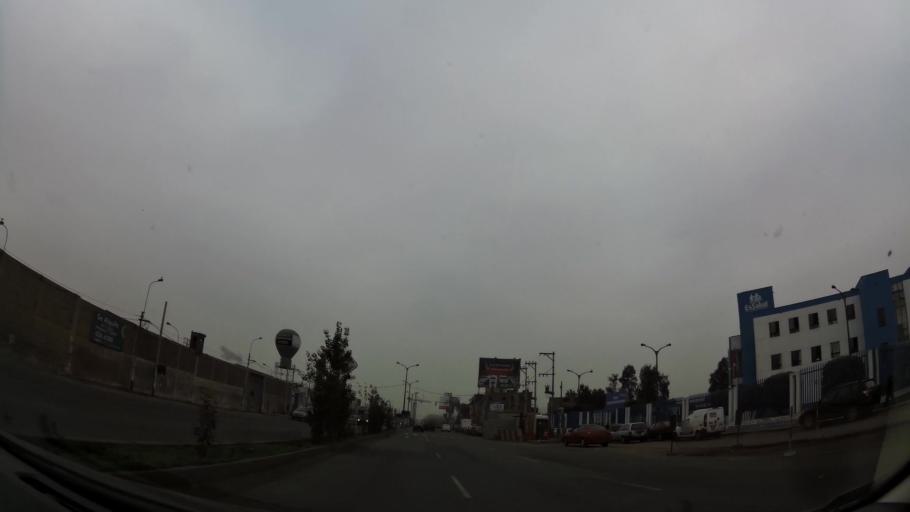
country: PE
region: Lima
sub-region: Lima
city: Vitarte
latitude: -12.0474
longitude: -76.9471
